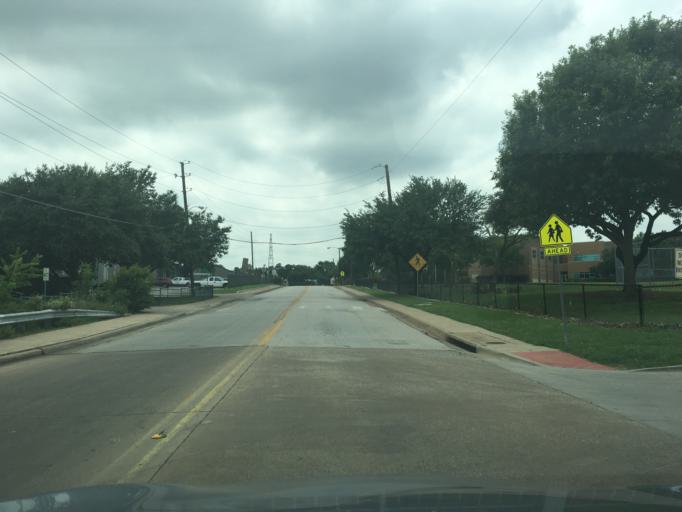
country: US
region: Texas
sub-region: Dallas County
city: Richardson
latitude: 32.9366
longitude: -96.7584
